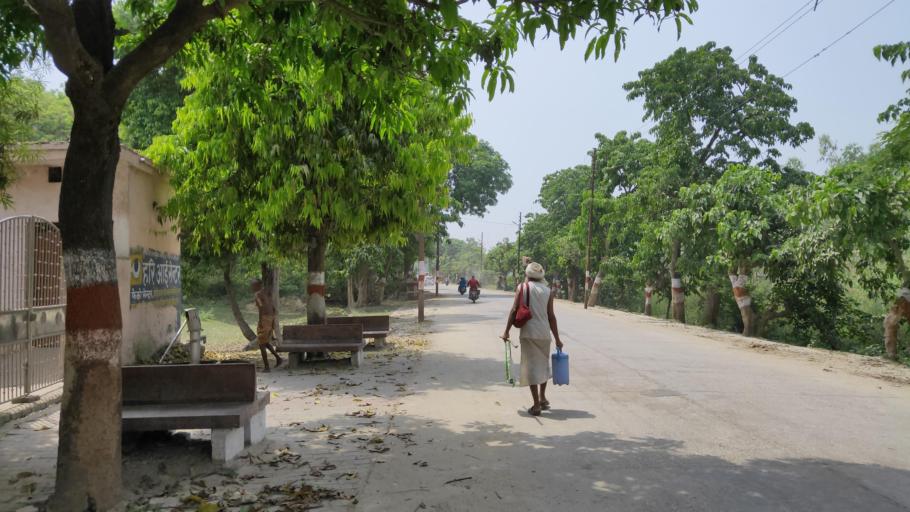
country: IN
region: Uttar Pradesh
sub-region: Faizabad
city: Ayodhya
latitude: 26.7858
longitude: 82.1799
